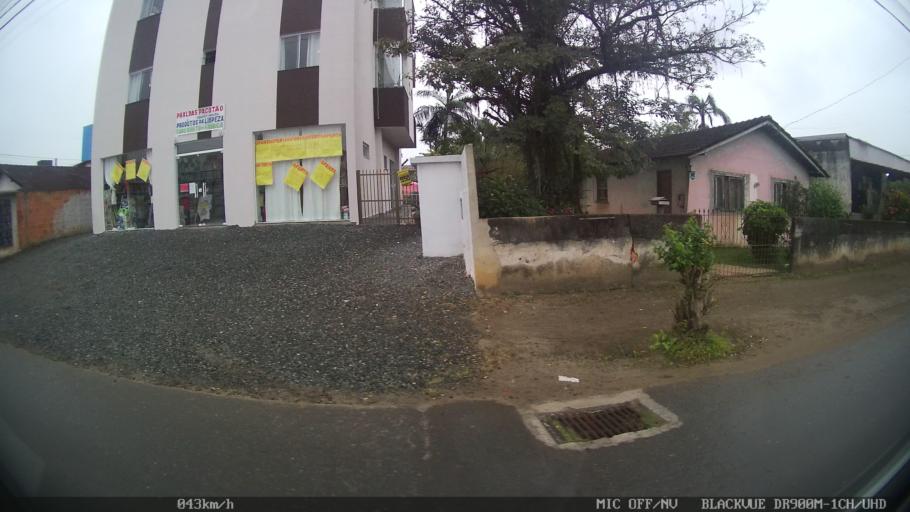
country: BR
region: Santa Catarina
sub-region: Joinville
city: Joinville
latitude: -26.2738
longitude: -48.8032
